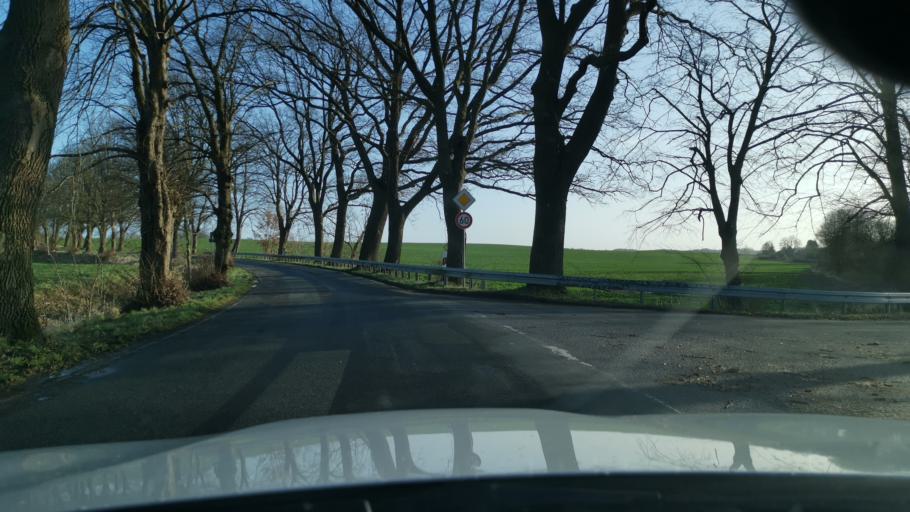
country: DE
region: Mecklenburg-Vorpommern
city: Tessin
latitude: 54.0135
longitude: 12.4190
